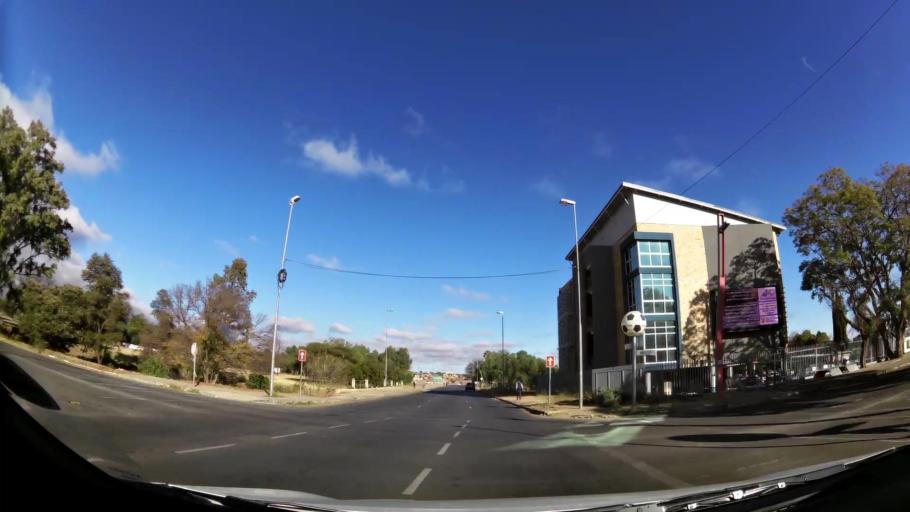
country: ZA
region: Limpopo
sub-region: Capricorn District Municipality
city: Polokwane
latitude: -23.9202
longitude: 29.4552
